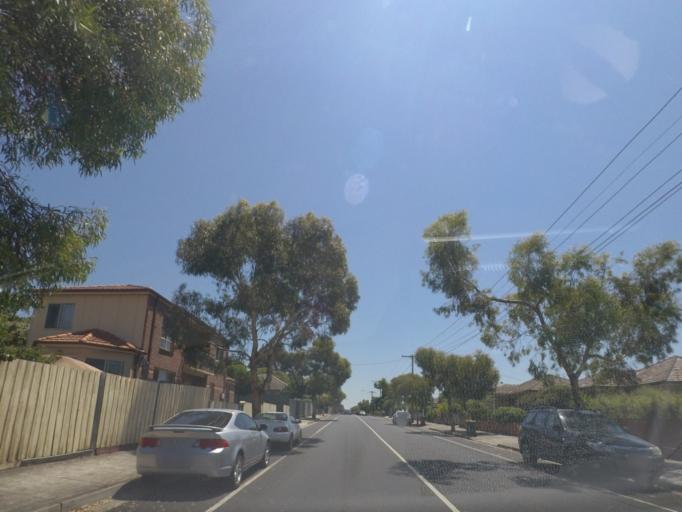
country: AU
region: Victoria
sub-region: Moreland
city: Hadfield
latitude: -37.7179
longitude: 144.9500
